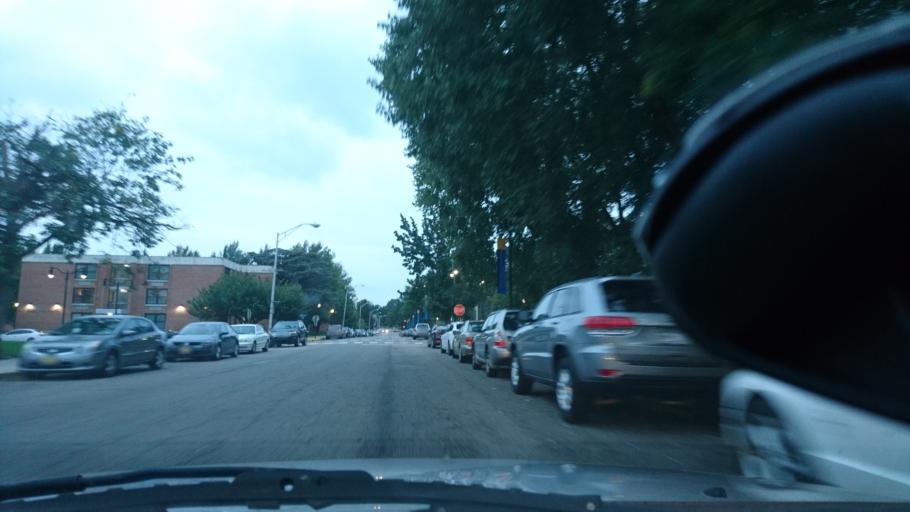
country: US
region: Pennsylvania
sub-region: Delaware County
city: Chester
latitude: 39.8608
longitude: -75.3579
